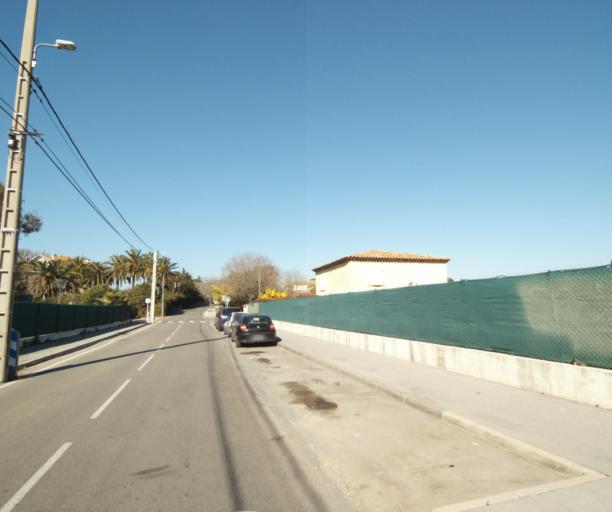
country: FR
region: Provence-Alpes-Cote d'Azur
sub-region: Departement des Alpes-Maritimes
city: Biot
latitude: 43.6005
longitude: 7.1014
